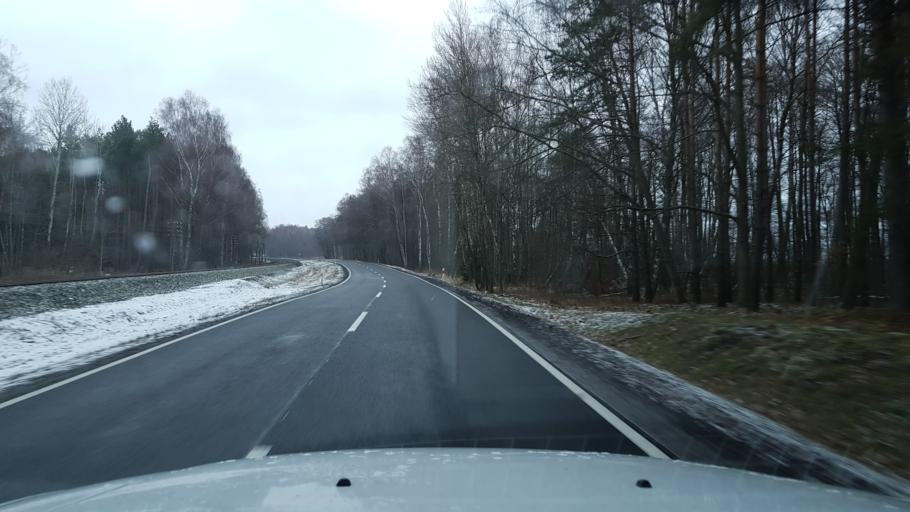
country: PL
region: West Pomeranian Voivodeship
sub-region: Powiat szczecinecki
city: Lubowo
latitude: 53.6058
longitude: 16.4423
